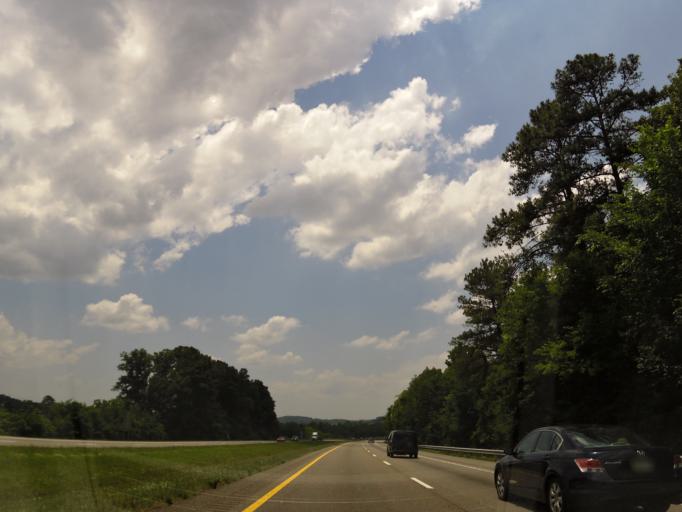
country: US
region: Tennessee
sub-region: Loudon County
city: Lenoir City
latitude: 35.8370
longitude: -84.2734
